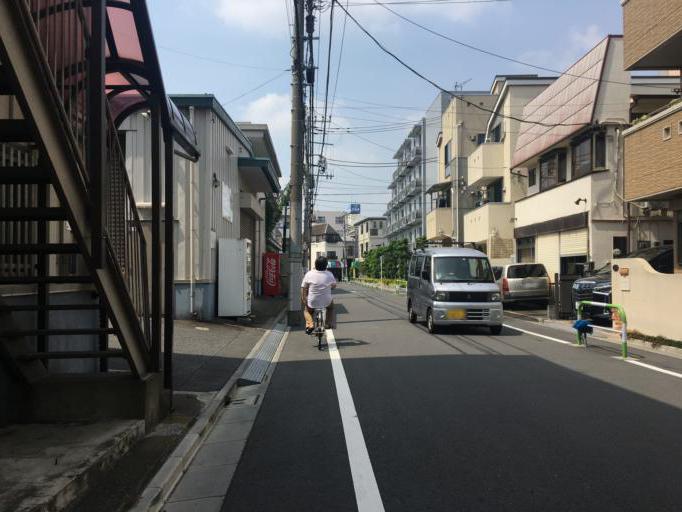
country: JP
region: Tokyo
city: Tokyo
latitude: 35.7332
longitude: 139.6929
